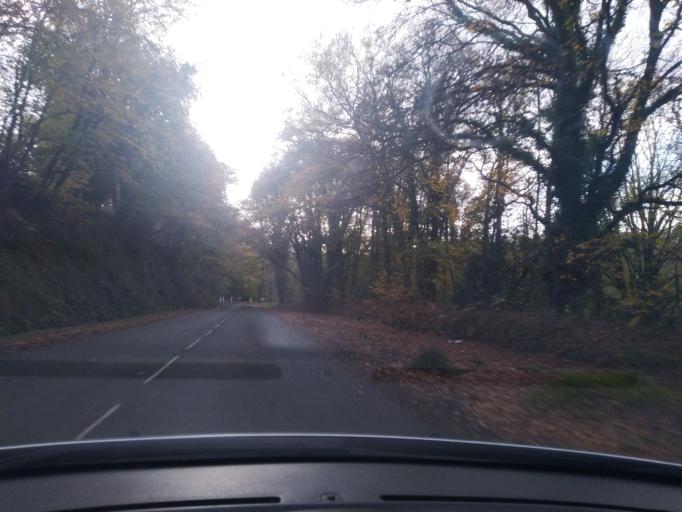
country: FR
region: Brittany
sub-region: Departement du Finistere
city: Plouigneau
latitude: 48.5707
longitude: -3.6440
